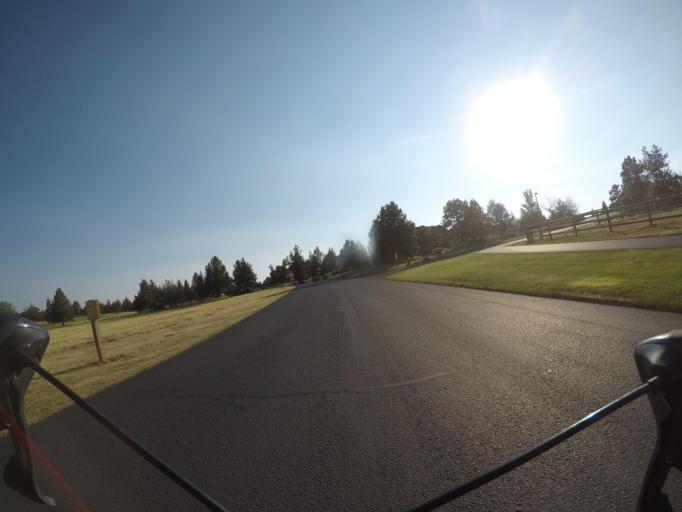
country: US
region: Oregon
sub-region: Deschutes County
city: Redmond
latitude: 44.2634
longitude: -121.2605
